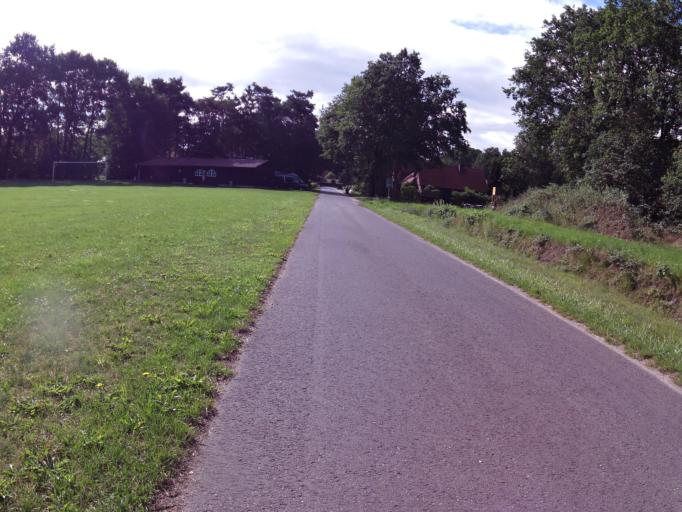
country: DE
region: Lower Saxony
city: Sandbostel
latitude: 53.4342
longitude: 9.1239
